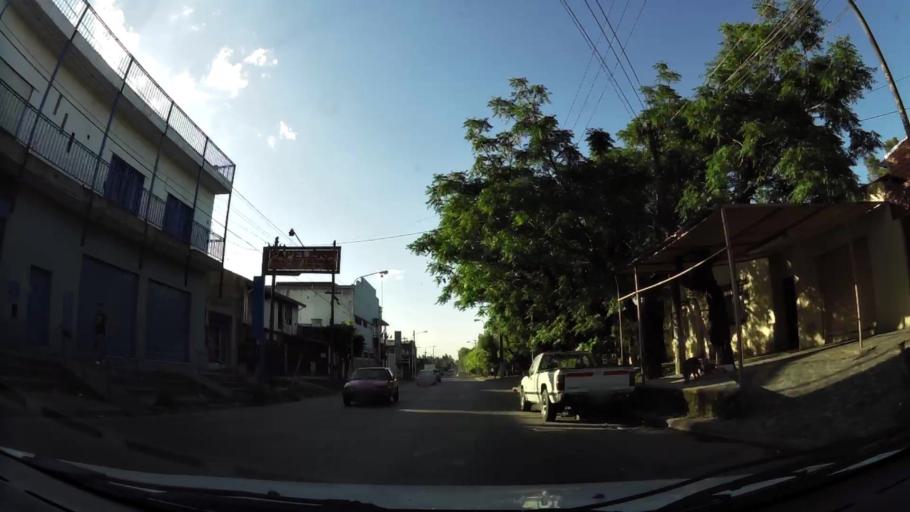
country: AR
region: Buenos Aires
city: Caseros
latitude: -34.5737
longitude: -58.5844
